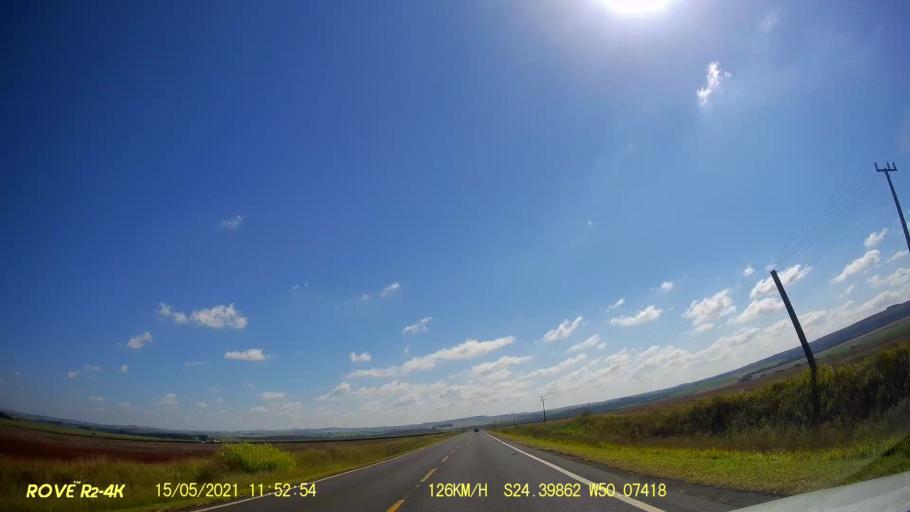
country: BR
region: Parana
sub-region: Pirai Do Sul
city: Pirai do Sul
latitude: -24.3986
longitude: -50.0743
